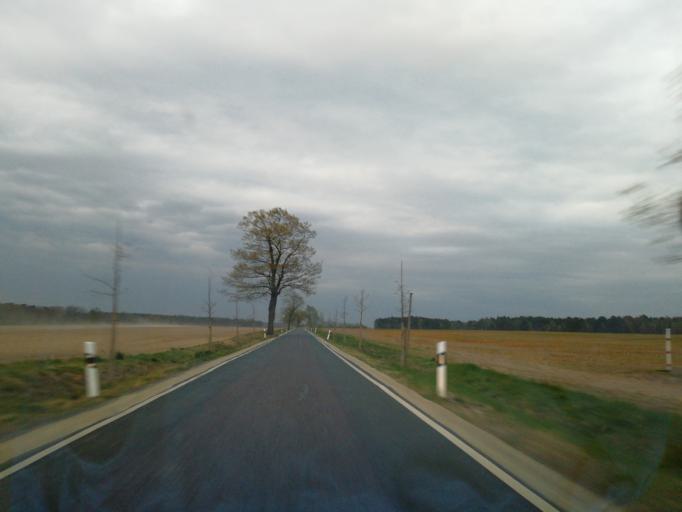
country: DE
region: Brandenburg
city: Calau
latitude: 51.7703
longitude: 13.8878
